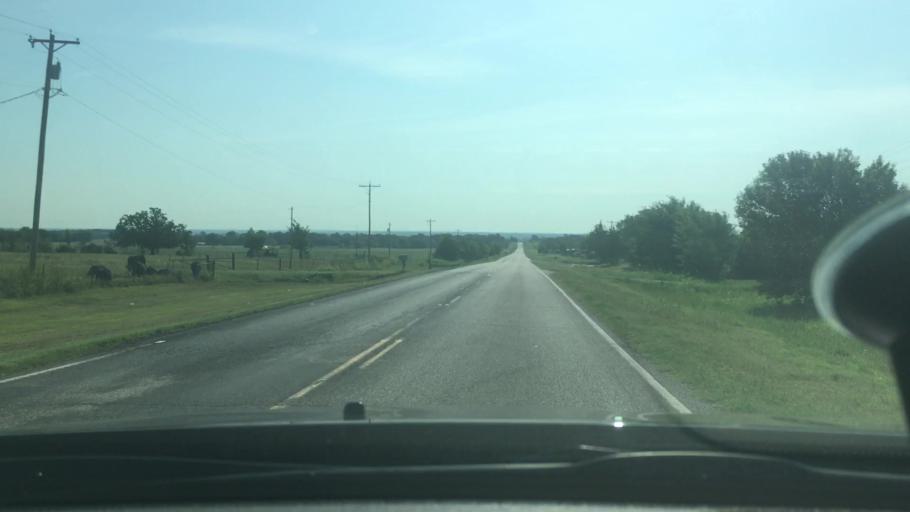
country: US
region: Oklahoma
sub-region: Garvin County
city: Wynnewood
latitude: 34.6518
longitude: -97.2434
